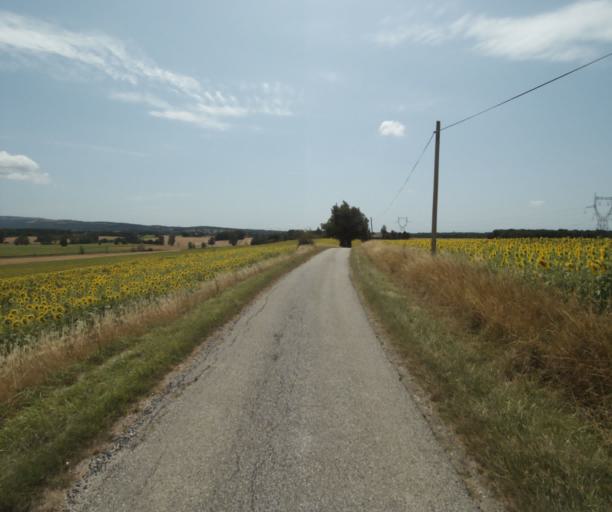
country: FR
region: Midi-Pyrenees
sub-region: Departement de la Haute-Garonne
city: Saint-Felix-Lauragais
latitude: 43.4155
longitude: 1.9115
